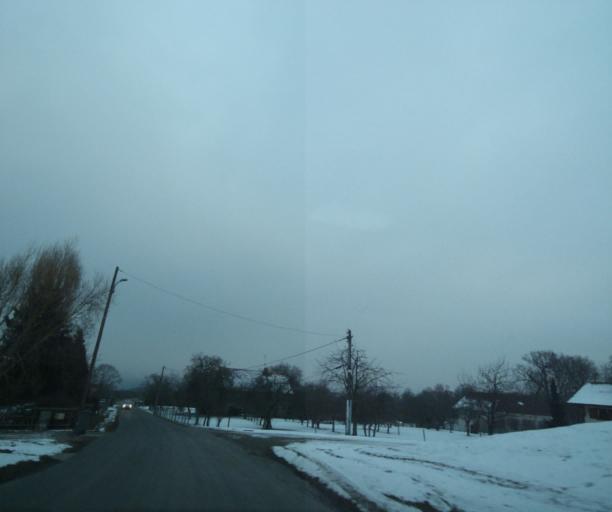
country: FR
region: Rhone-Alpes
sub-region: Departement de la Haute-Savoie
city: Reignier-Esery
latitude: 46.1428
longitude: 6.2447
